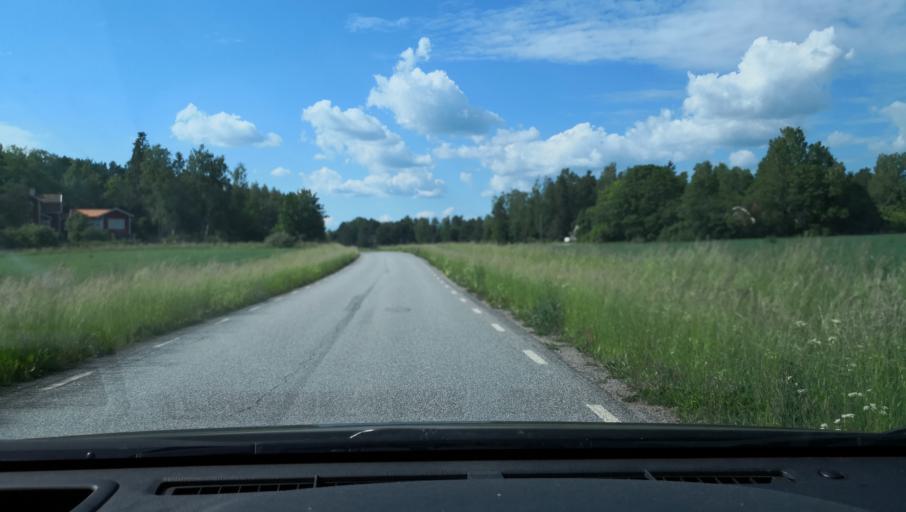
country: SE
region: Uppsala
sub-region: Enkopings Kommun
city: Orsundsbro
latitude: 59.8216
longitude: 17.3257
